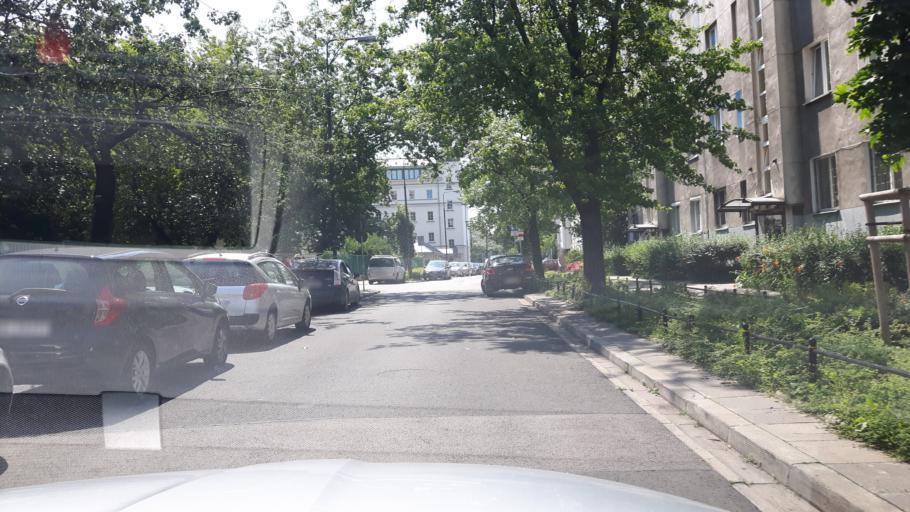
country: PL
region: Masovian Voivodeship
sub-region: Warszawa
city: Srodmiescie
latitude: 52.2243
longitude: 21.0373
